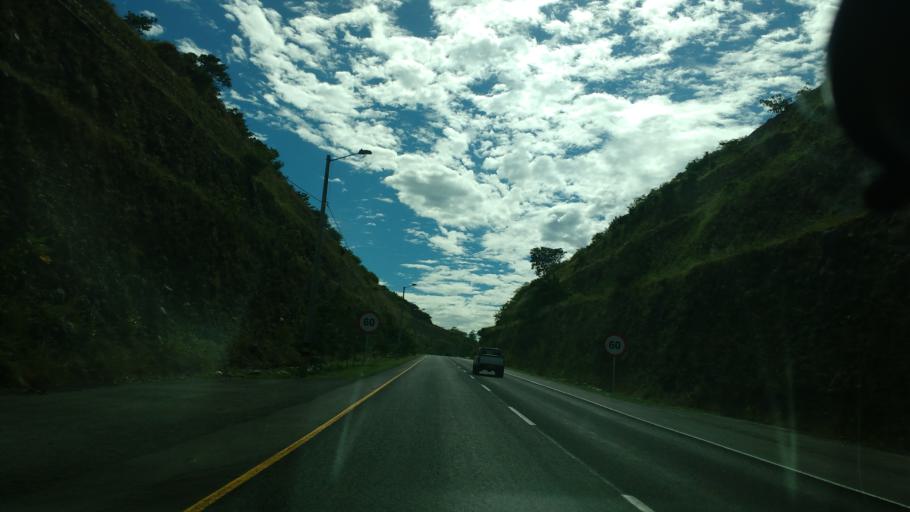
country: CO
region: Tolima
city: Valle de San Juan
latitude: 4.2921
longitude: -75.0373
